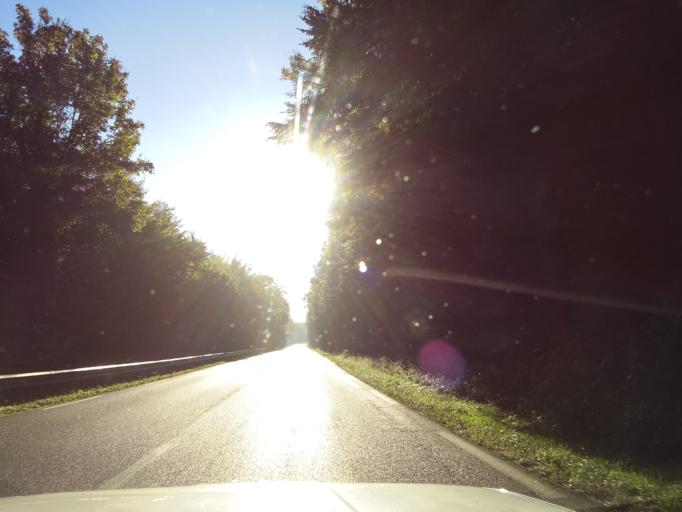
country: FR
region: Rhone-Alpes
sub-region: Departement de l'Ain
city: Saint-Sorlin-en-Bugey
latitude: 45.8705
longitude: 5.3726
